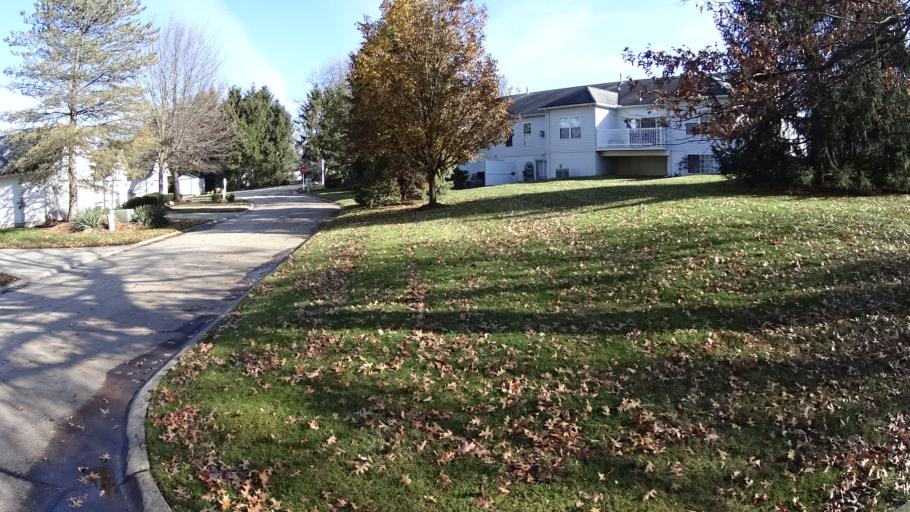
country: US
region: Ohio
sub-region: Lorain County
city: North Ridgeville
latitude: 41.4002
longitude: -81.9940
